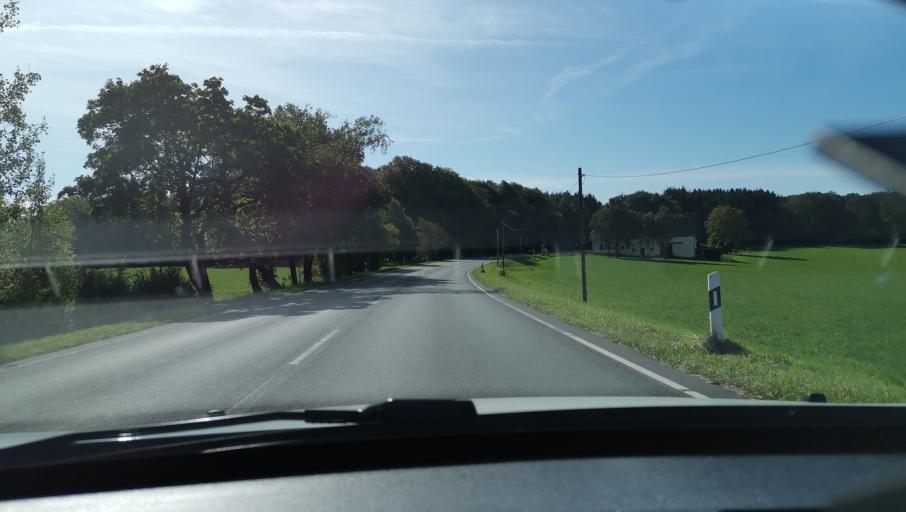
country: DE
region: North Rhine-Westphalia
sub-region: Regierungsbezirk Arnsberg
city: Breckerfeld
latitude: 51.2373
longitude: 7.4704
